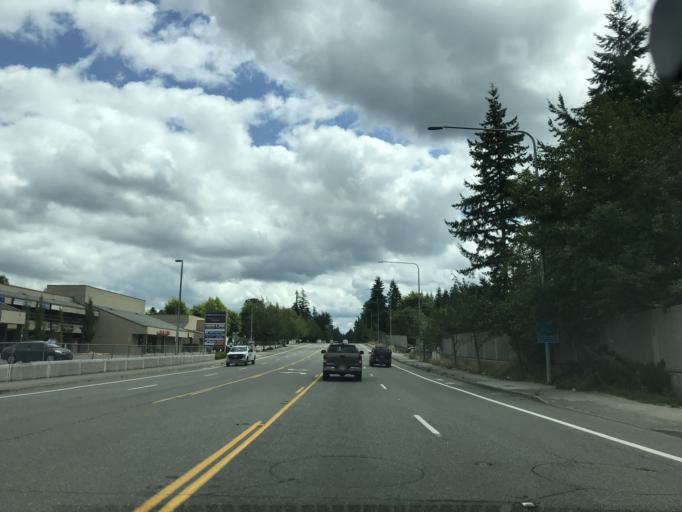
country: US
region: Washington
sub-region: King County
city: Fairwood
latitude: 47.4443
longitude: -122.1495
